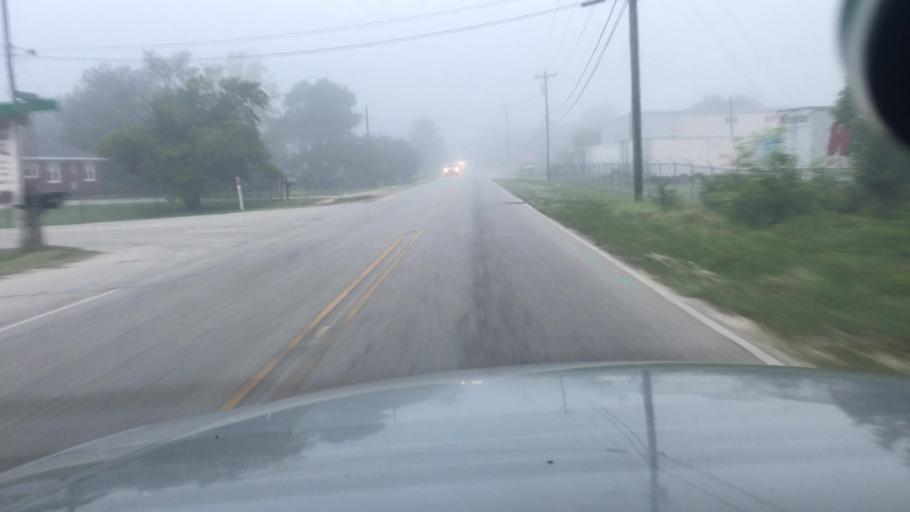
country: US
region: North Carolina
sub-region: Cumberland County
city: Fayetteville
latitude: 35.0137
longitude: -78.9007
